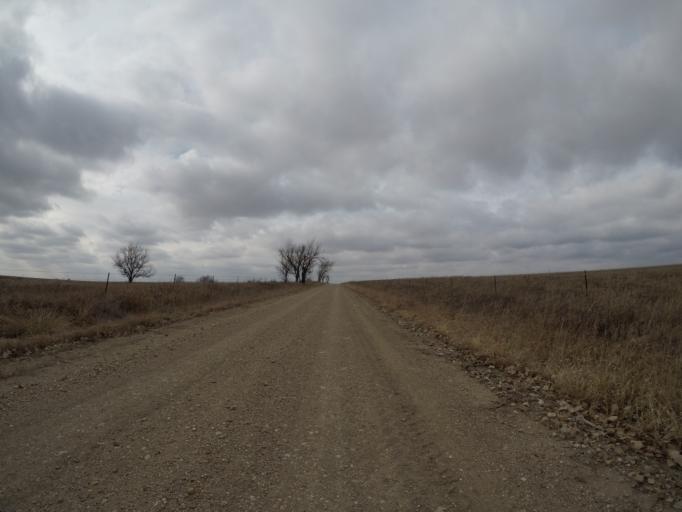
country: US
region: Kansas
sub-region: Morris County
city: Council Grove
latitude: 38.7244
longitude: -96.2147
